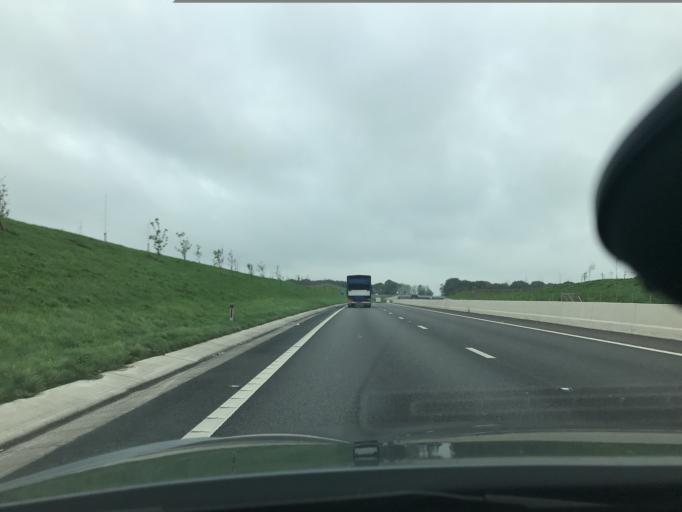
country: GB
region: England
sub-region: Cheshire East
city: Mere
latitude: 53.3415
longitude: -2.4148
